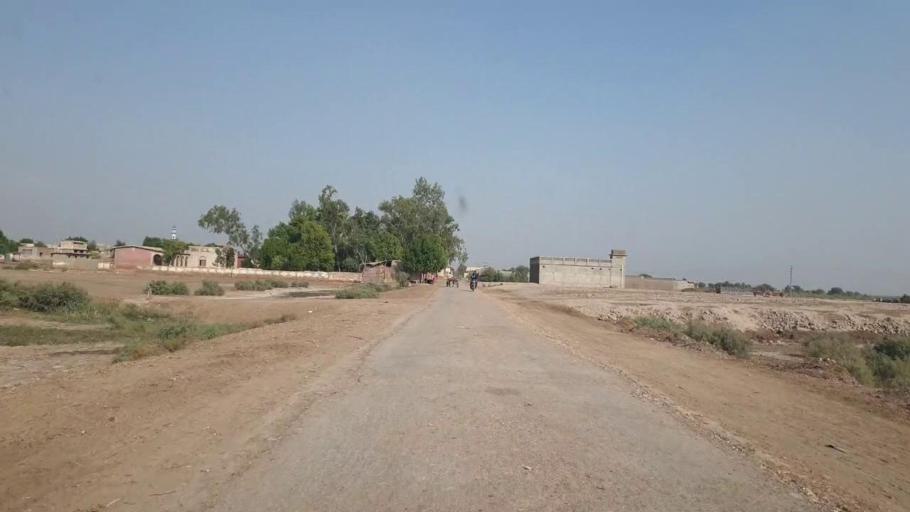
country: PK
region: Sindh
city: Sinjhoro
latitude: 26.0556
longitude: 68.8422
